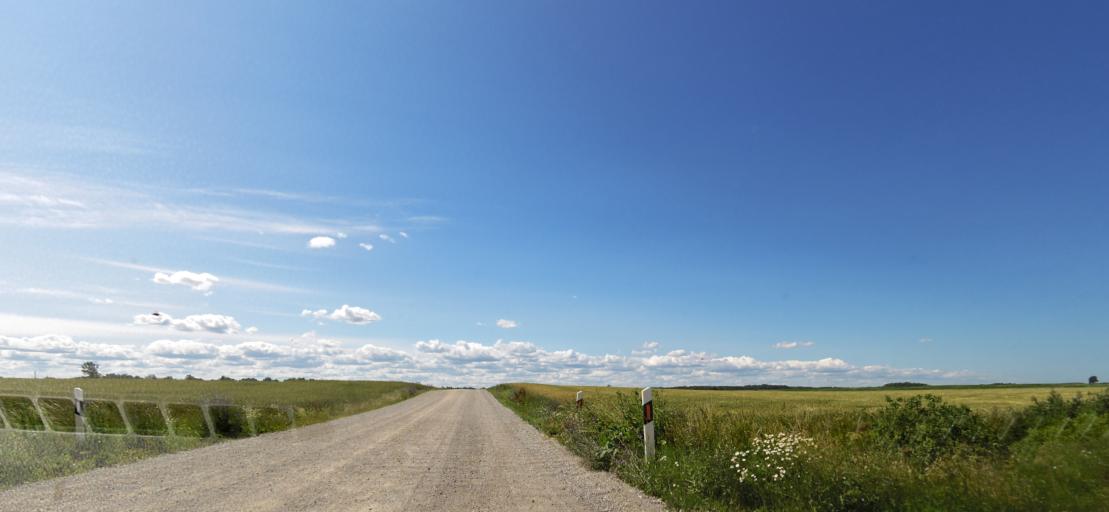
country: LT
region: Panevezys
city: Pasvalys
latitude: 56.2510
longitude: 24.3507
